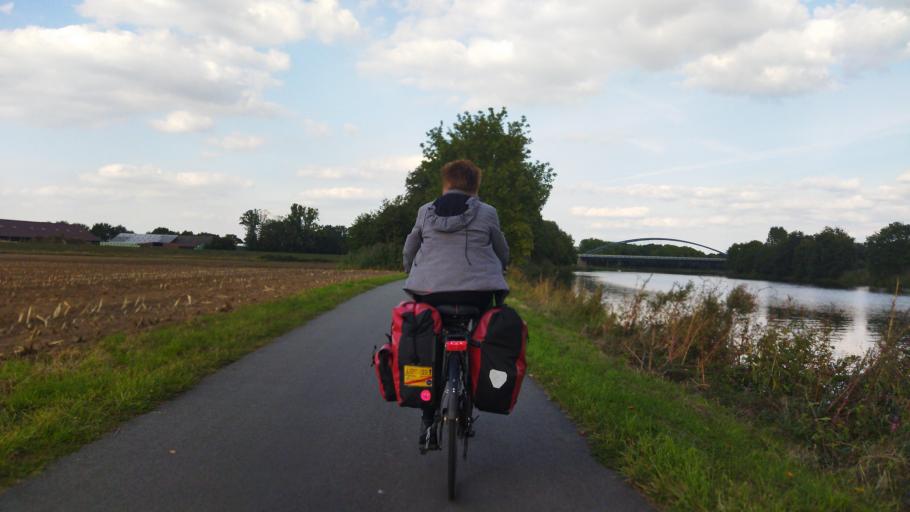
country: DE
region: Lower Saxony
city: Dersum
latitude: 52.9775
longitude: 7.2986
